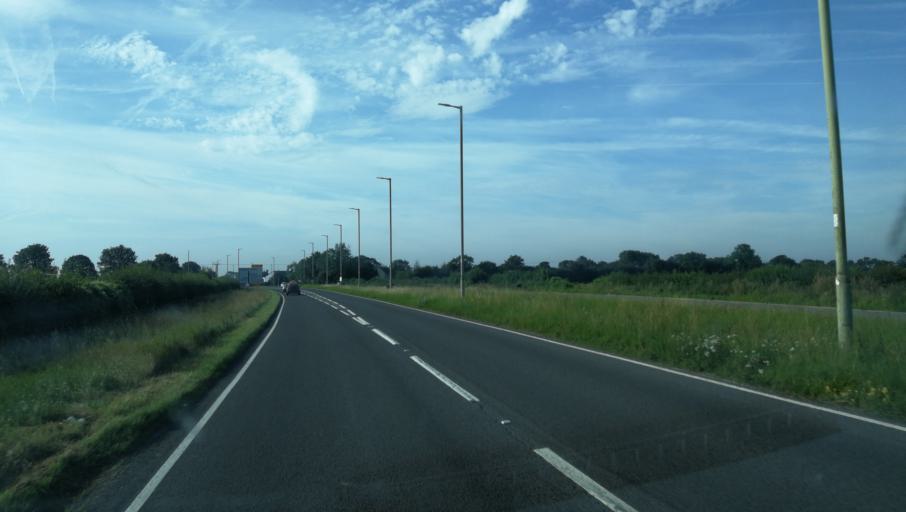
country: GB
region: England
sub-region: Oxfordshire
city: Woodstock
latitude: 51.8732
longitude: -1.3294
